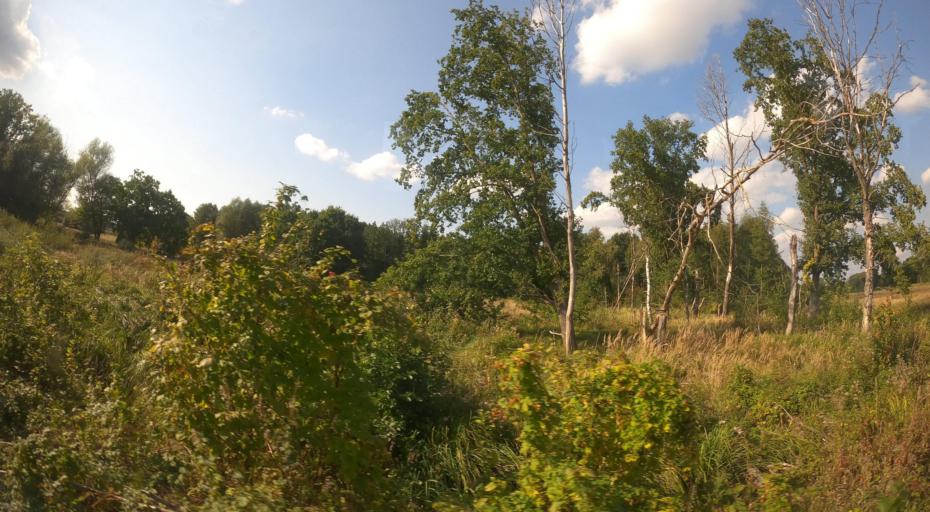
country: PL
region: Lubusz
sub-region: Powiat zielonogorski
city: Swidnica
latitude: 51.8787
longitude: 15.3240
